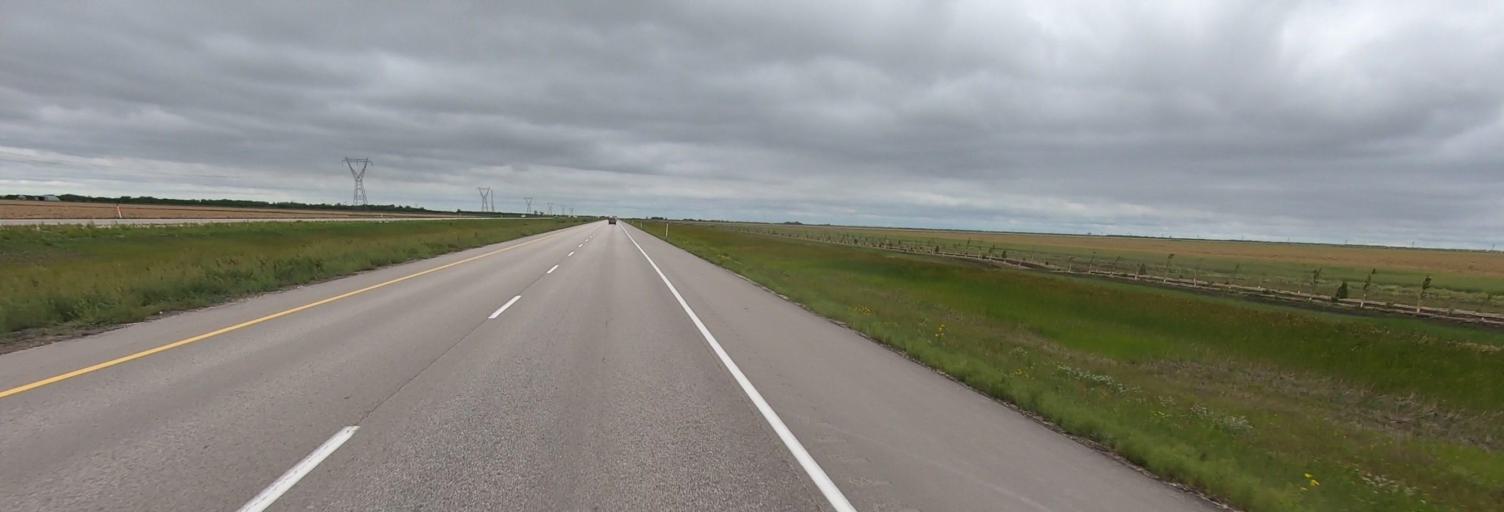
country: CA
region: Manitoba
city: Headingley
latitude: 49.8871
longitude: -97.6065
